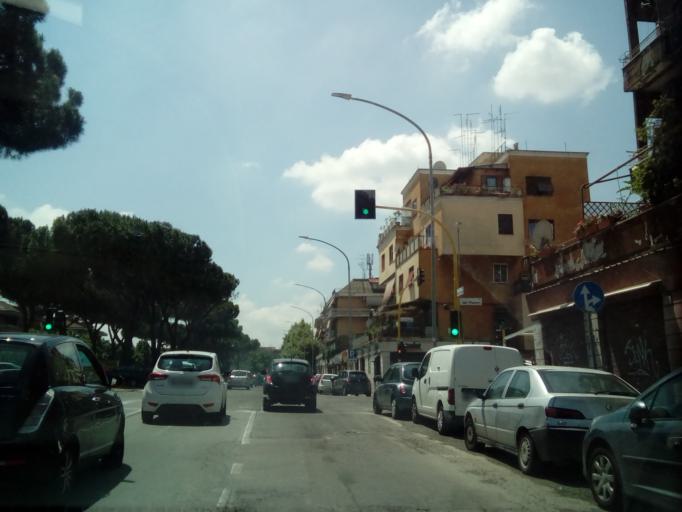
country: IT
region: Latium
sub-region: Citta metropolitana di Roma Capitale
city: Rome
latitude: 41.8812
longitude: 12.5729
